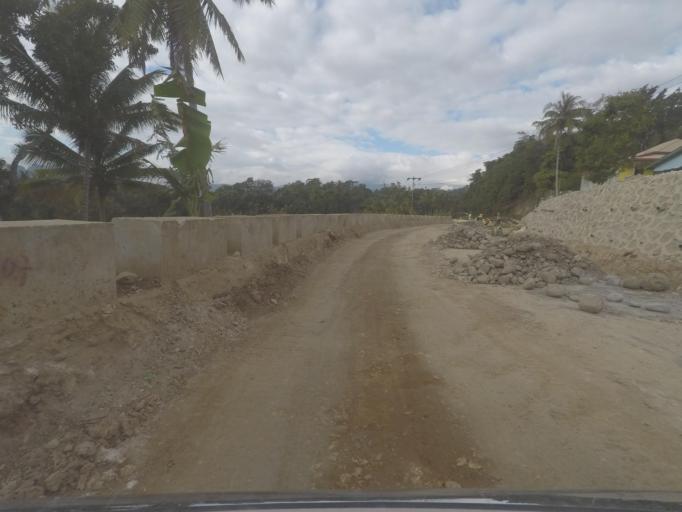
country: TL
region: Baucau
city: Venilale
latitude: -8.6071
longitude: 126.3826
